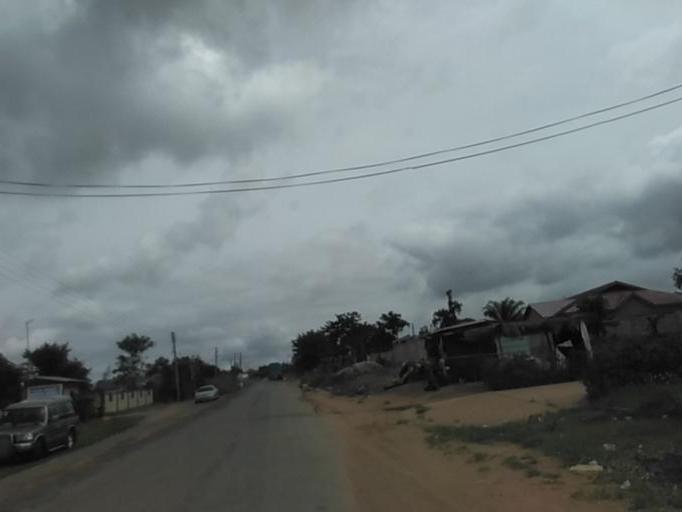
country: GH
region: Ashanti
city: Mamponteng
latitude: 6.7865
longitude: -1.4670
